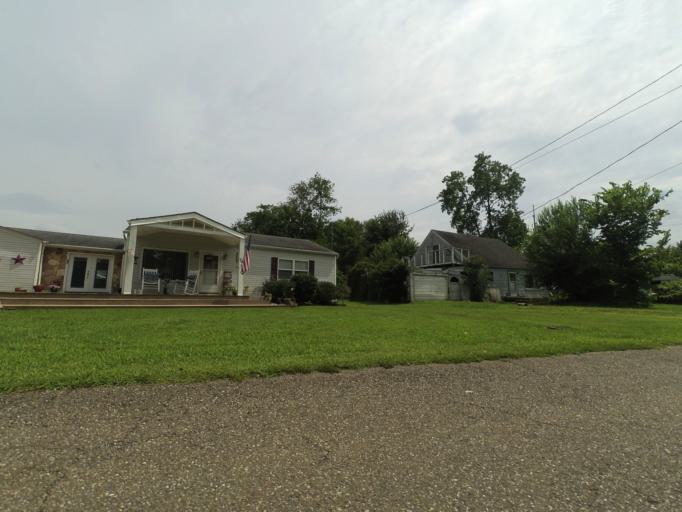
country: US
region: West Virginia
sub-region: Cabell County
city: Huntington
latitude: 38.4247
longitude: -82.4758
